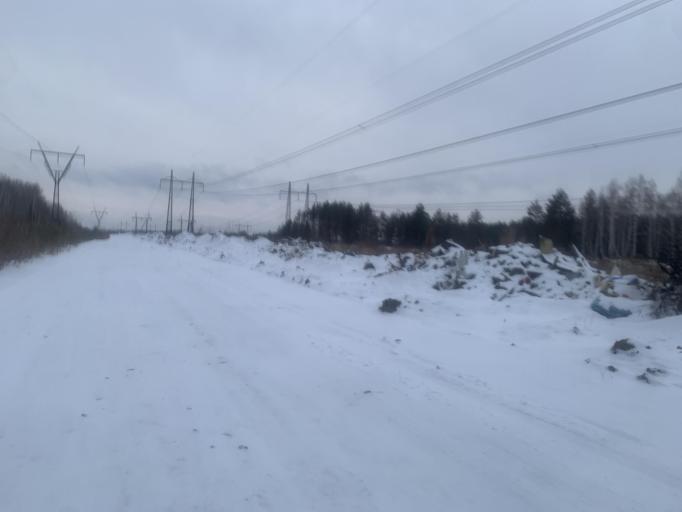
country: RU
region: Chelyabinsk
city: Roshchino
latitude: 55.1968
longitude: 61.2613
